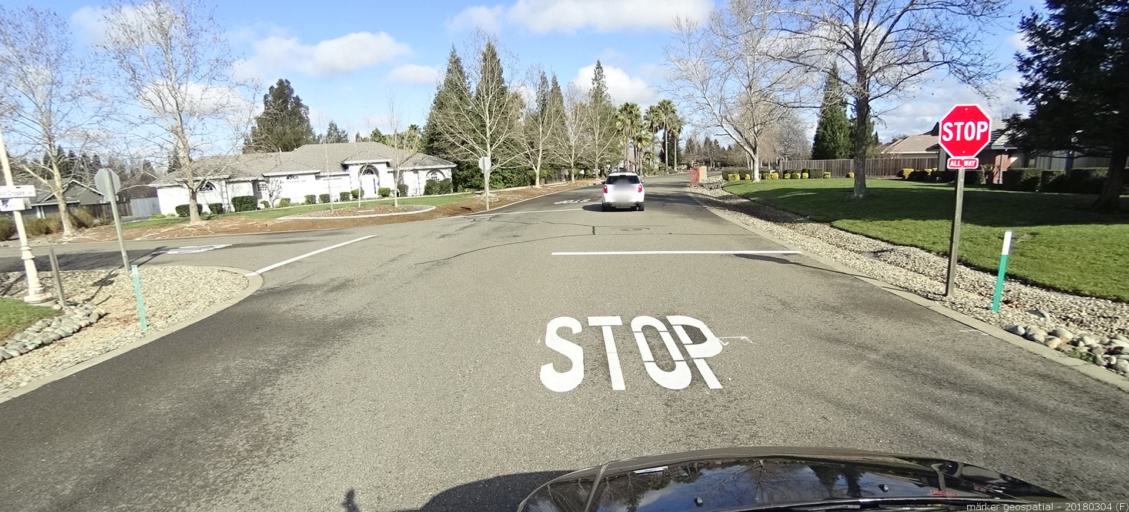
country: US
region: California
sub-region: Sacramento County
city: Vineyard
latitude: 38.4580
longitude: -121.3072
